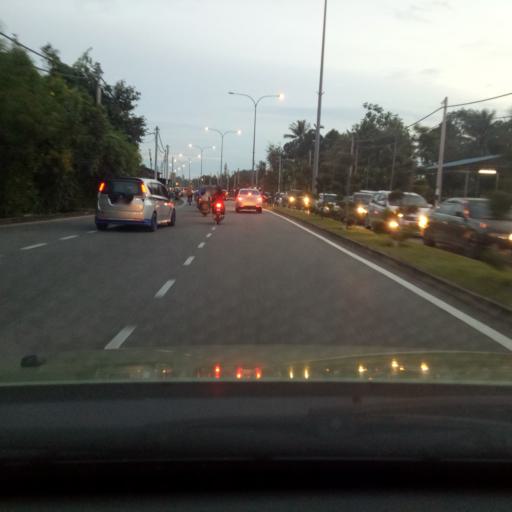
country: MY
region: Kedah
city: Alor Setar
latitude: 6.1167
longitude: 100.3755
